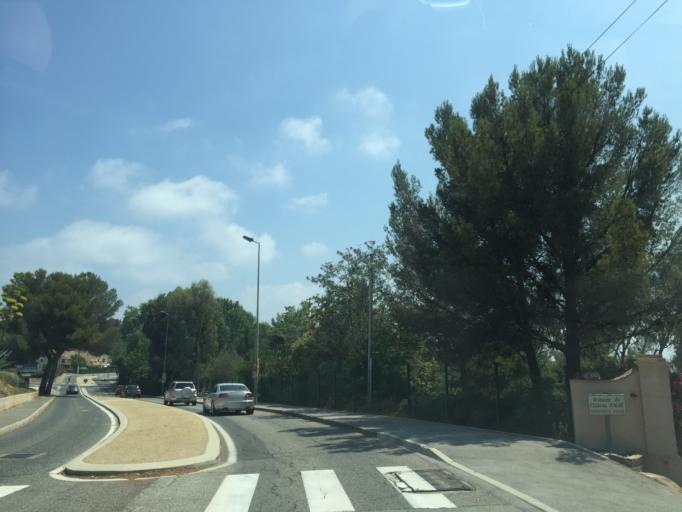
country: FR
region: Provence-Alpes-Cote d'Azur
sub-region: Departement du Var
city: Saint-Raphael
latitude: 43.4319
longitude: 6.8693
